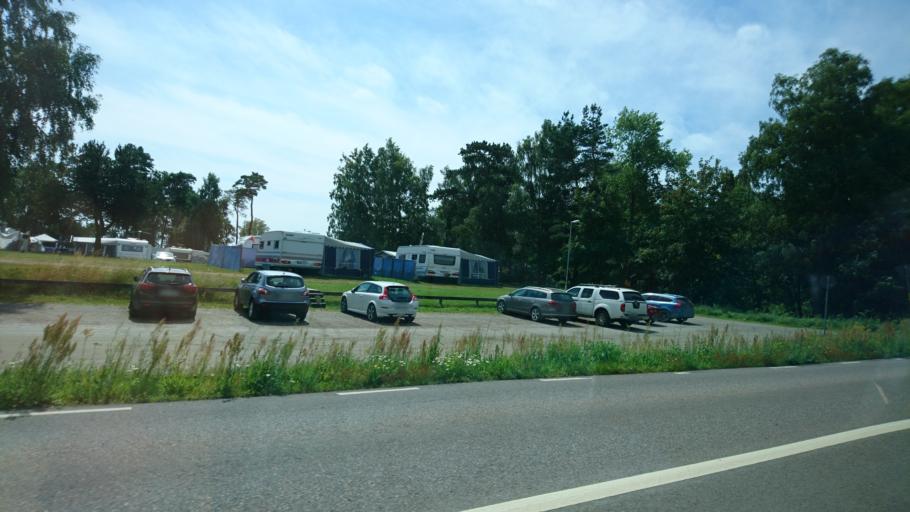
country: SE
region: Skane
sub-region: Skurups Kommun
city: Skivarp
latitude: 55.3864
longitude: 13.4978
